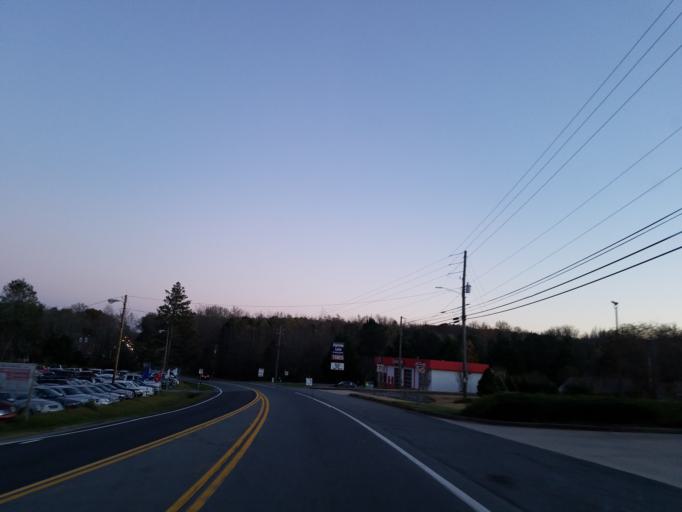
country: US
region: Georgia
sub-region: Dawson County
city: Dawsonville
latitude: 34.4159
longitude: -84.1130
